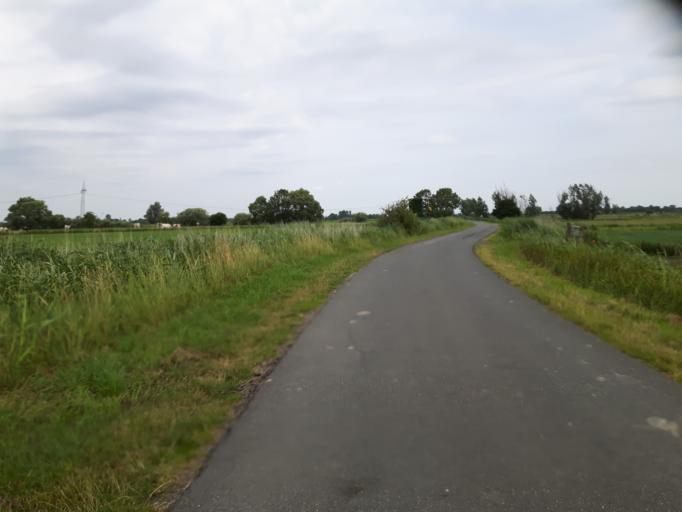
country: DE
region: Lower Saxony
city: Varel
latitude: 53.3710
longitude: 8.2093
